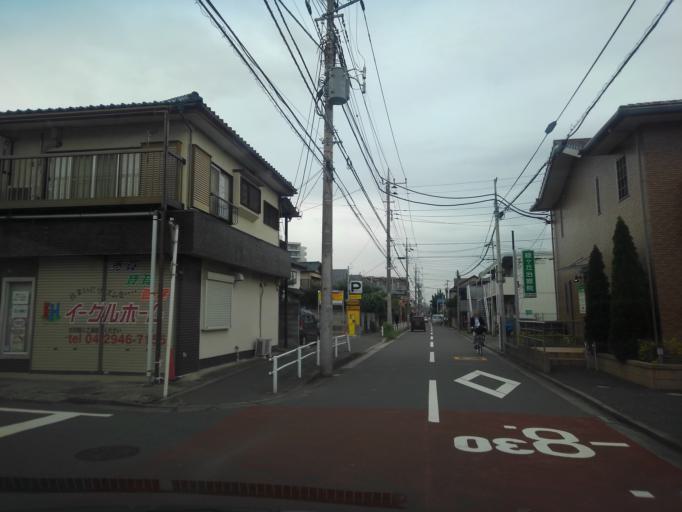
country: JP
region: Saitama
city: Tokorozawa
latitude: 35.8013
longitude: 139.4416
